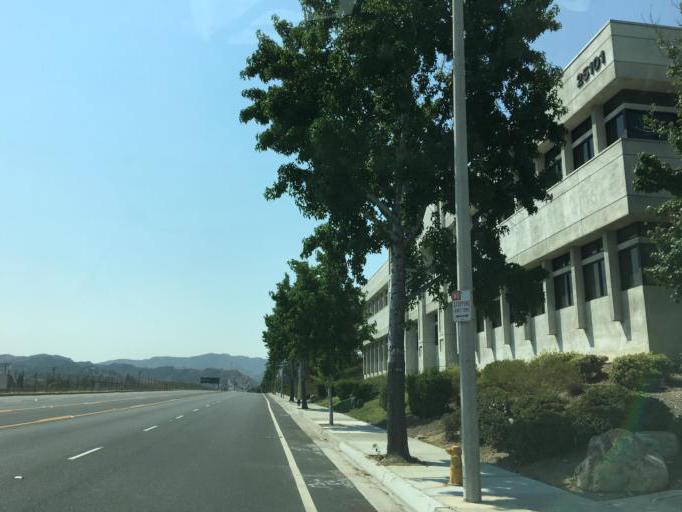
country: US
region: California
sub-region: Los Angeles County
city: Santa Clarita
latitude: 34.3744
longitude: -118.5633
